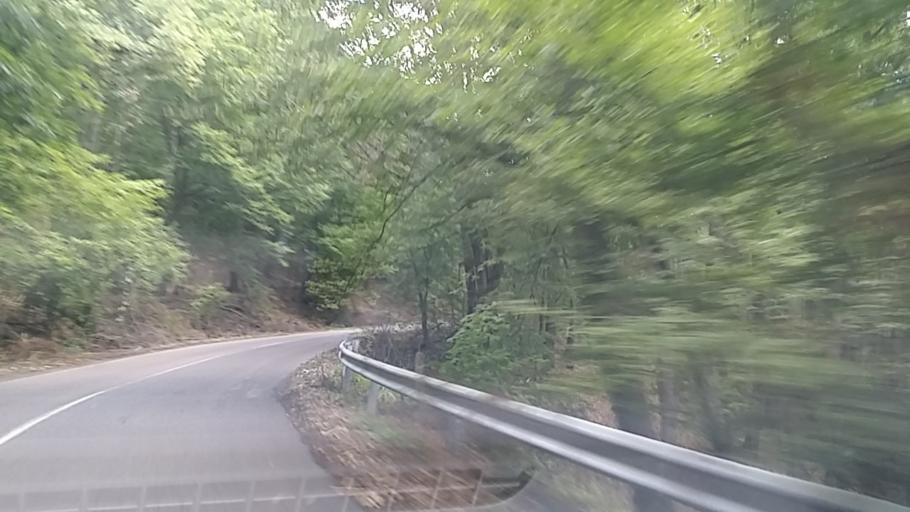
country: HU
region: Nograd
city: Batonyterenye
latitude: 47.9006
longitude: 19.8341
